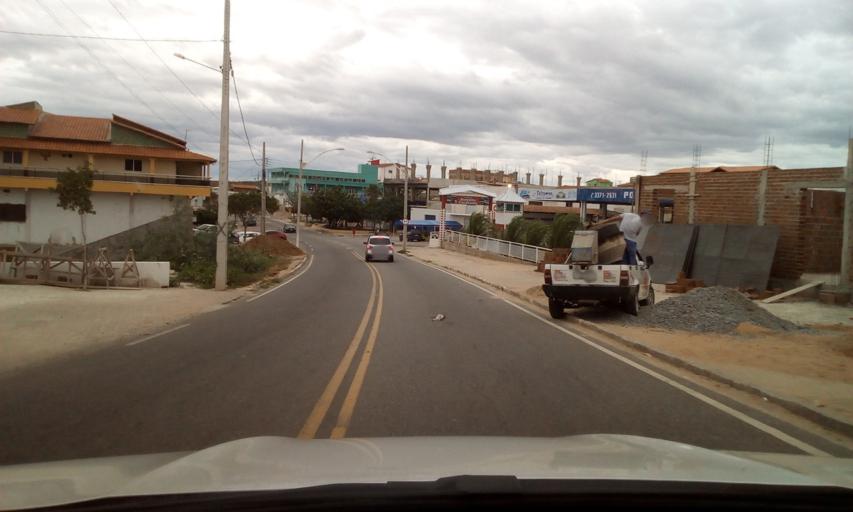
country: BR
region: Paraiba
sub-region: Picui
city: Picui
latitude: -6.5094
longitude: -36.3406
